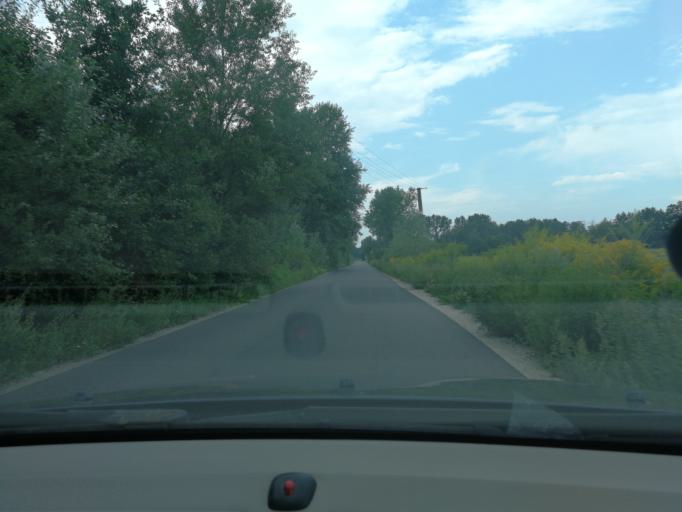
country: PL
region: Masovian Voivodeship
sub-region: Powiat warszawski zachodni
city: Bieniewice
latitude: 52.1090
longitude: 20.5550
